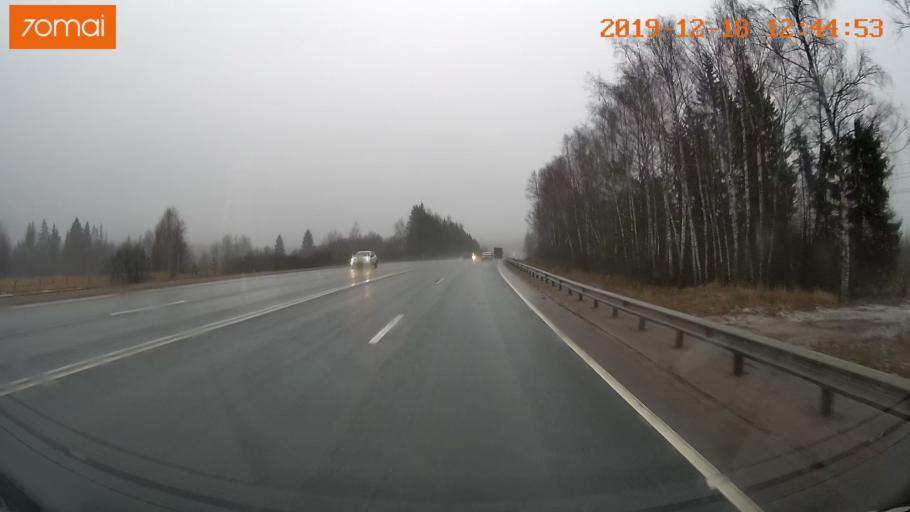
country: RU
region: Moskovskaya
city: Klin
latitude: 56.2250
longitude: 36.6519
